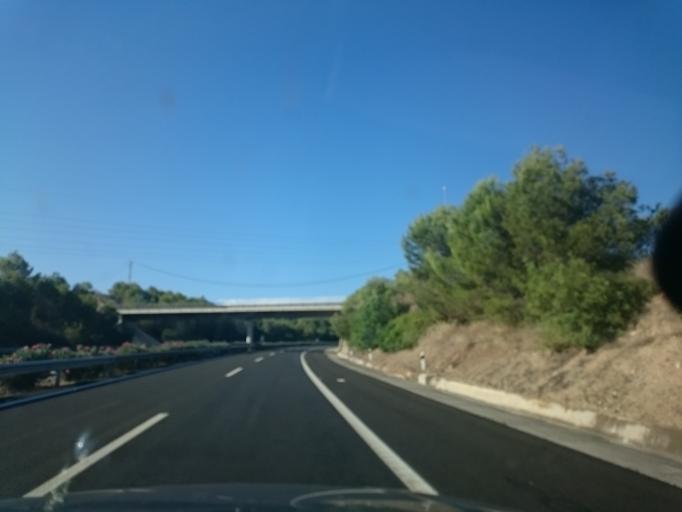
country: ES
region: Catalonia
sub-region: Provincia de Barcelona
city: Cubelles
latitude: 41.2371
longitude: 1.6820
